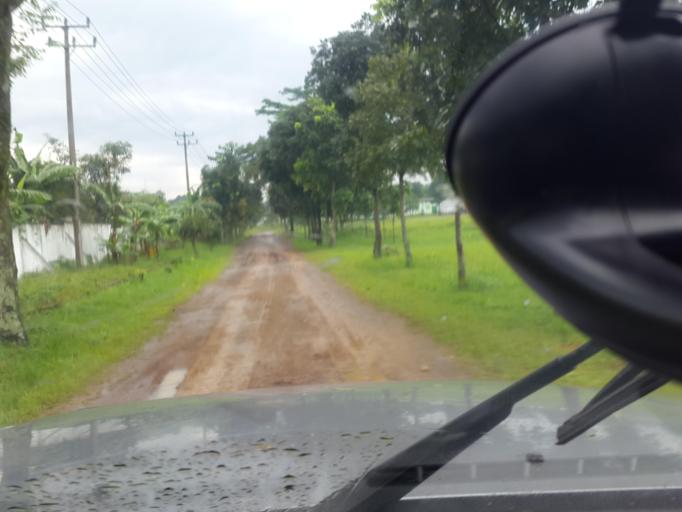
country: ID
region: West Java
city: Bandung
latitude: -6.9130
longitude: 107.6852
